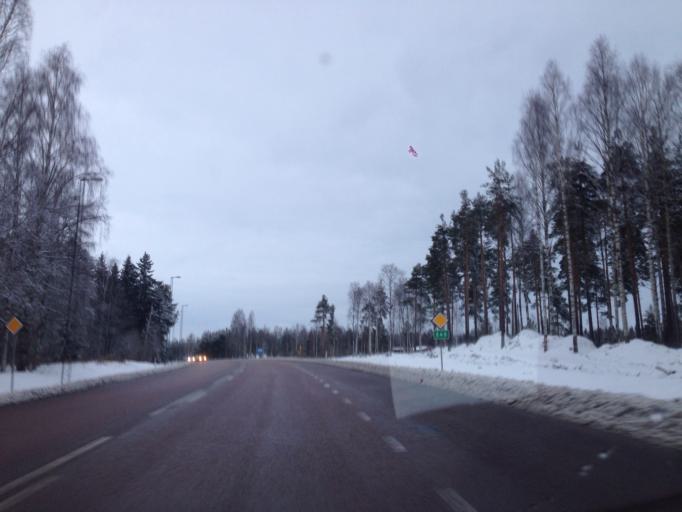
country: SE
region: Dalarna
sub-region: Mora Kommun
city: Mora
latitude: 61.0111
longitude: 14.5903
